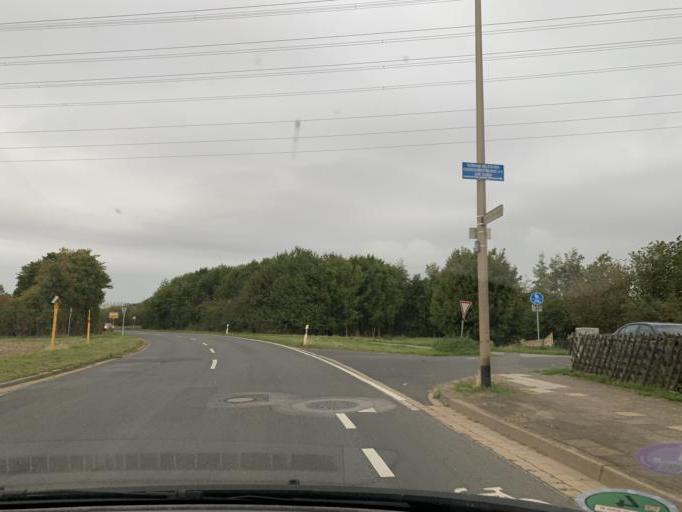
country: DE
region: North Rhine-Westphalia
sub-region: Regierungsbezirk Koln
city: Niederzier
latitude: 50.8338
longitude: 6.4408
